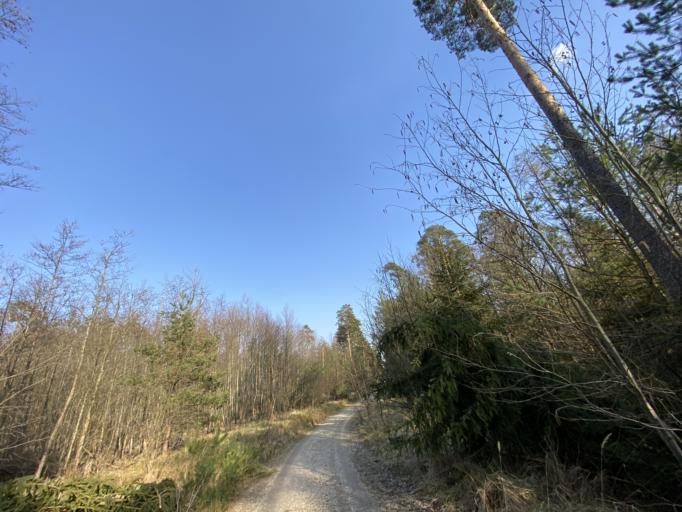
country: DE
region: Bavaria
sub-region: Regierungsbezirk Mittelfranken
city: Buckenhof
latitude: 49.5503
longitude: 11.0659
